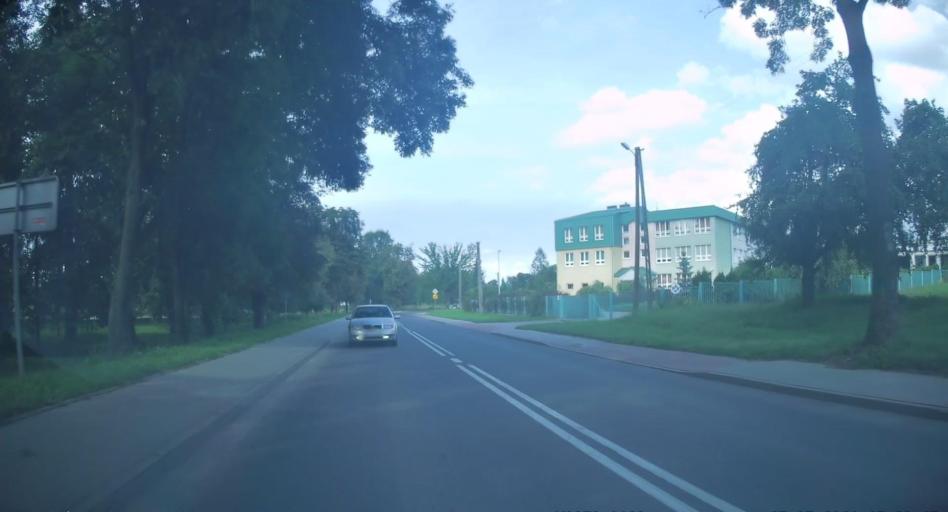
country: PL
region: Lodz Voivodeship
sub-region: Powiat tomaszowski
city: Rzeczyca
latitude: 51.5971
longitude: 20.2925
